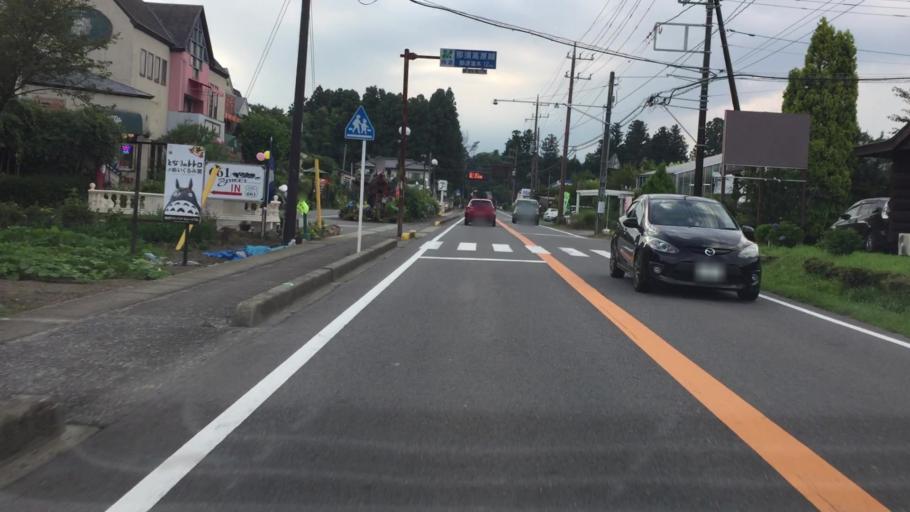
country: JP
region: Tochigi
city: Kuroiso
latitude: 37.0072
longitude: 140.0325
